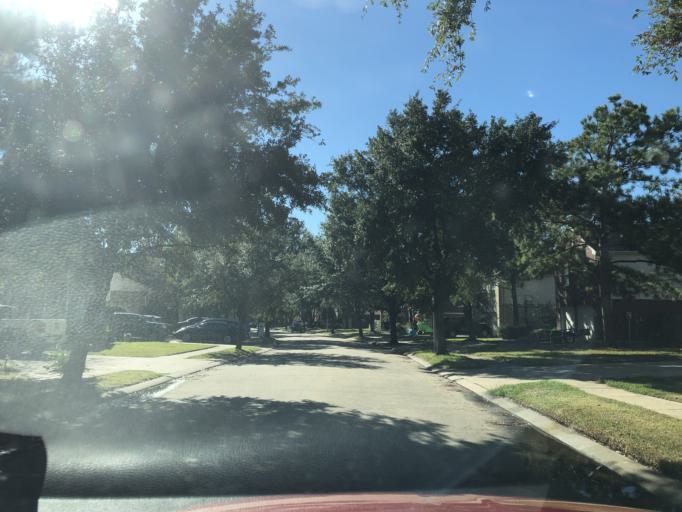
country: US
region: Texas
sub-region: Harris County
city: Oak Cliff Place
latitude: 29.9362
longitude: -95.6600
